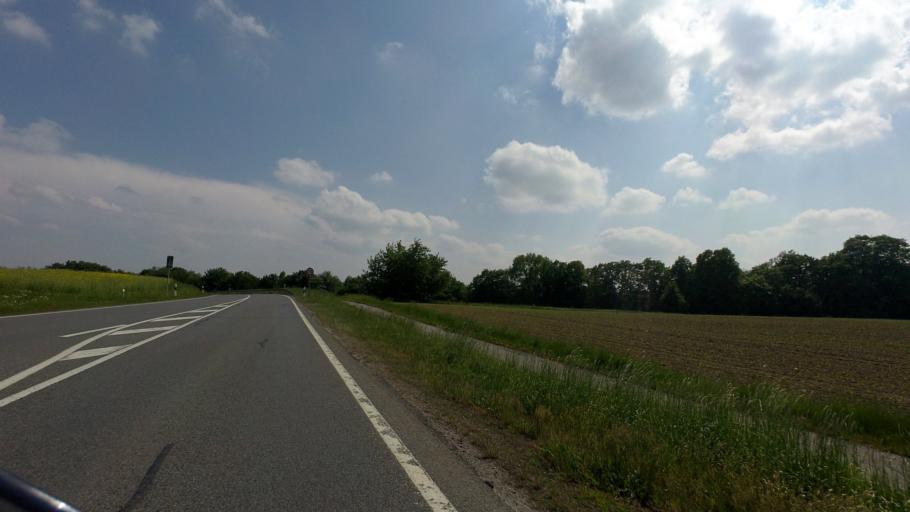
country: DE
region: Saxony
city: Weissenberg
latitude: 51.1934
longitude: 14.6722
